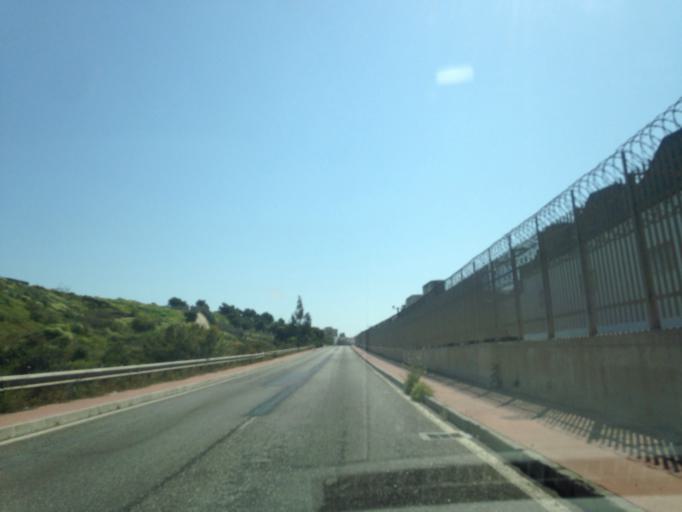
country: ES
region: Andalusia
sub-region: Provincia de Malaga
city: Malaga
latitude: 36.7013
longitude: -4.4848
